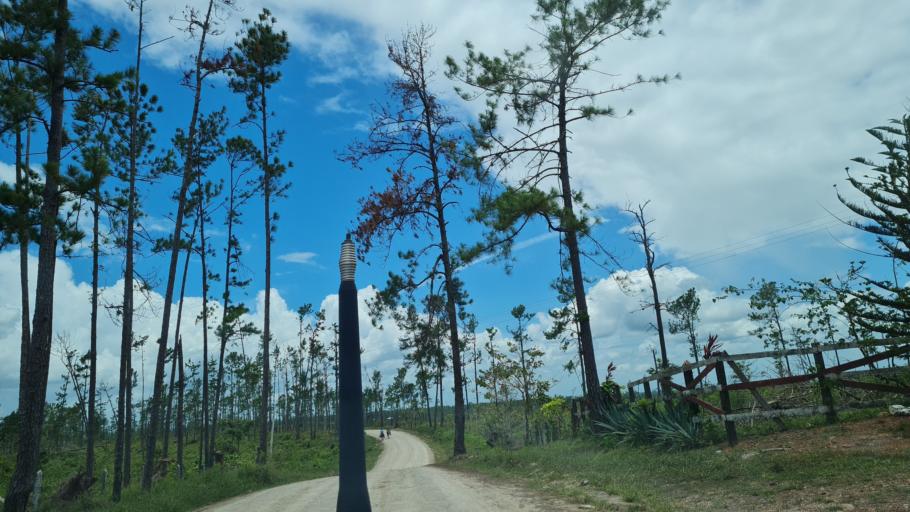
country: NI
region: Atlantico Sur
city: La Cruz de Rio Grande
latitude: 13.5725
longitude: -84.3223
